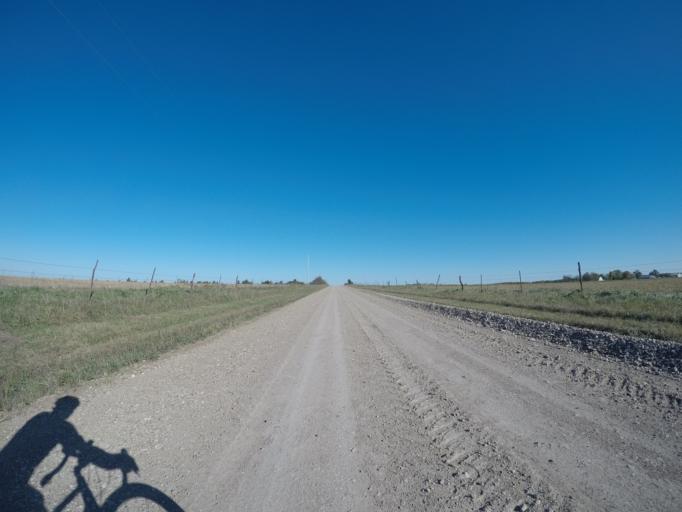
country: US
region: Kansas
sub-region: Morris County
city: Council Grove
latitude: 38.8377
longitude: -96.4088
